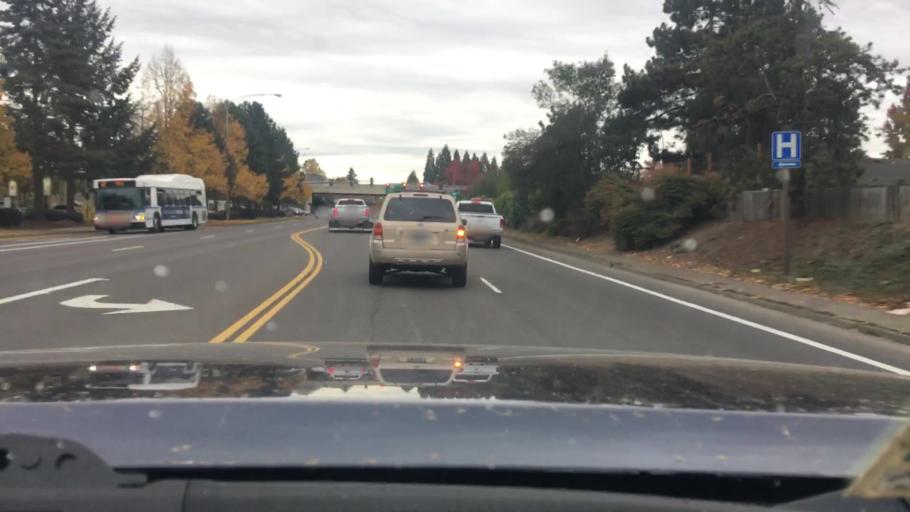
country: US
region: Oregon
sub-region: Lane County
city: Eugene
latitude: 44.0897
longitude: -123.0678
